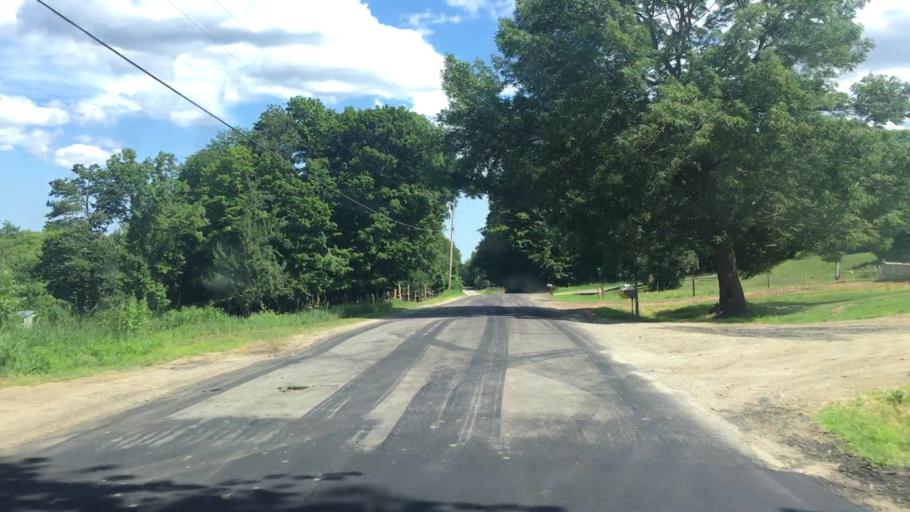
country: US
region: Maine
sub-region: Franklin County
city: Chesterville
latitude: 44.5681
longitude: -70.1467
